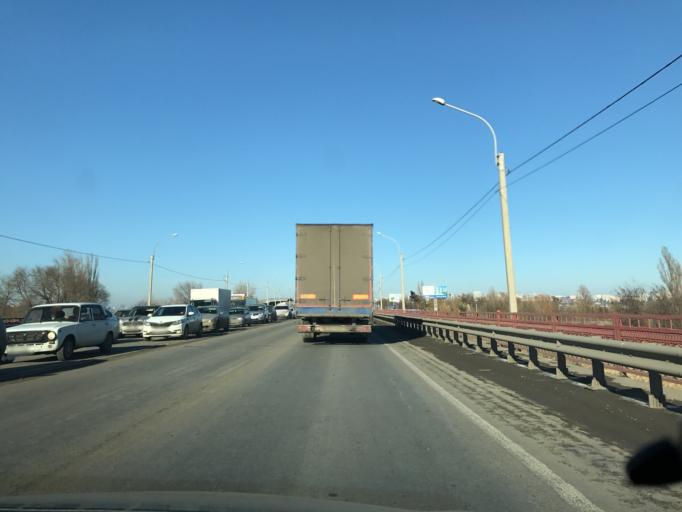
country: RU
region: Rostov
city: Bataysk
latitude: 47.1806
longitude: 39.7399
